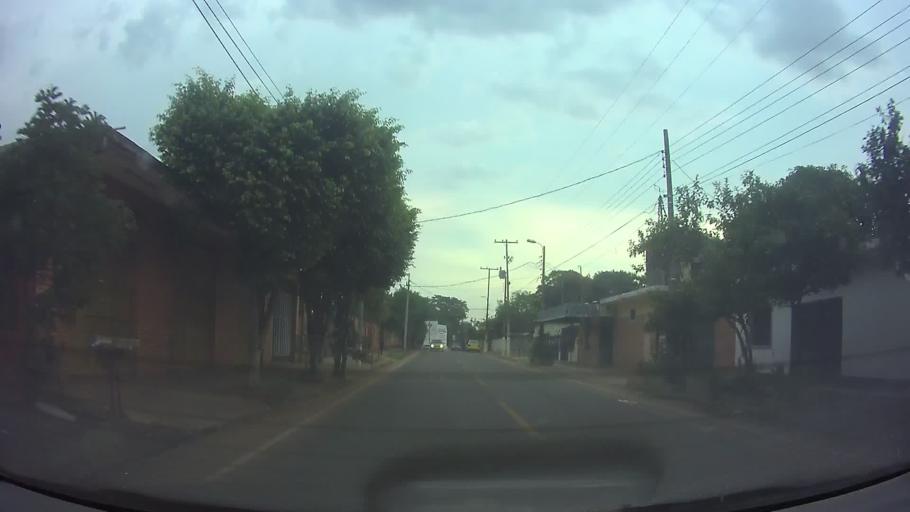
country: PY
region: Central
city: San Lorenzo
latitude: -25.2749
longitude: -57.4779
